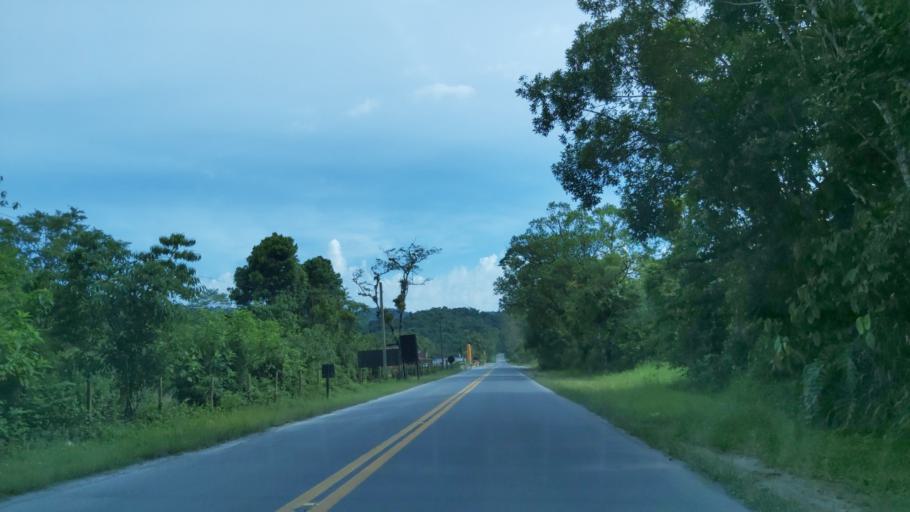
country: BR
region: Sao Paulo
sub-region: Miracatu
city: Miracatu
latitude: -24.0634
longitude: -47.5909
